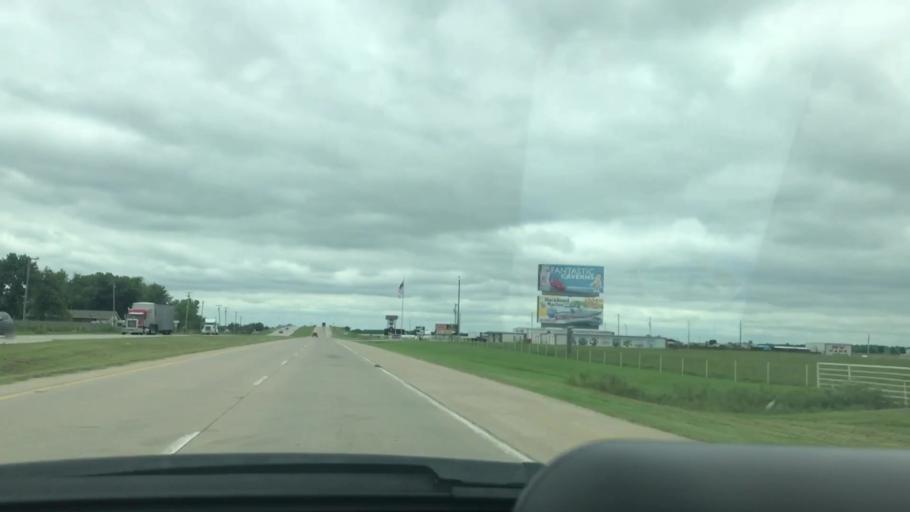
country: US
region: Oklahoma
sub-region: Craig County
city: Vinita
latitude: 36.5506
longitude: -95.2201
